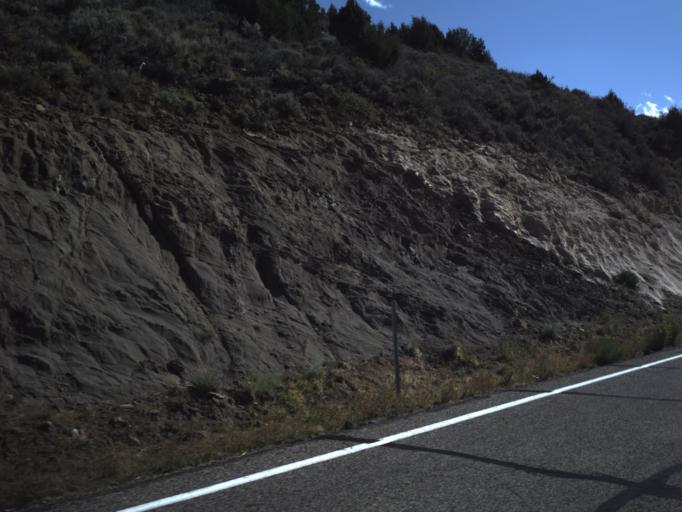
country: US
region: Utah
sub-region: Garfield County
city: Panguitch
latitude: 37.7578
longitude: -112.5609
